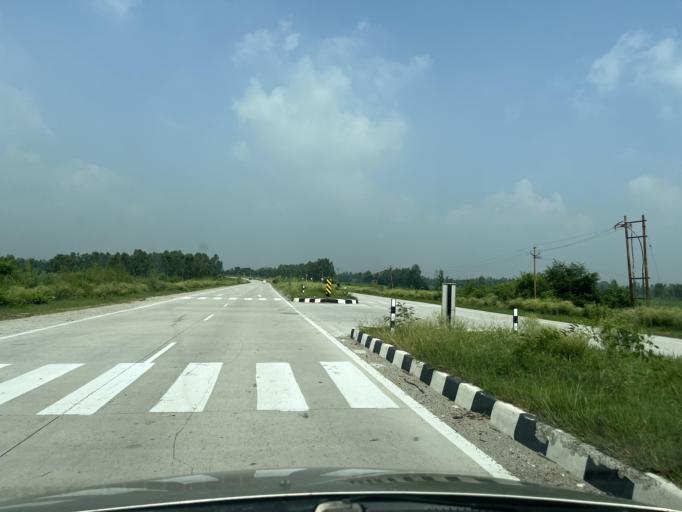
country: IN
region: Uttarakhand
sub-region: Udham Singh Nagar
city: Kashipur
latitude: 29.1650
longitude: 78.9895
